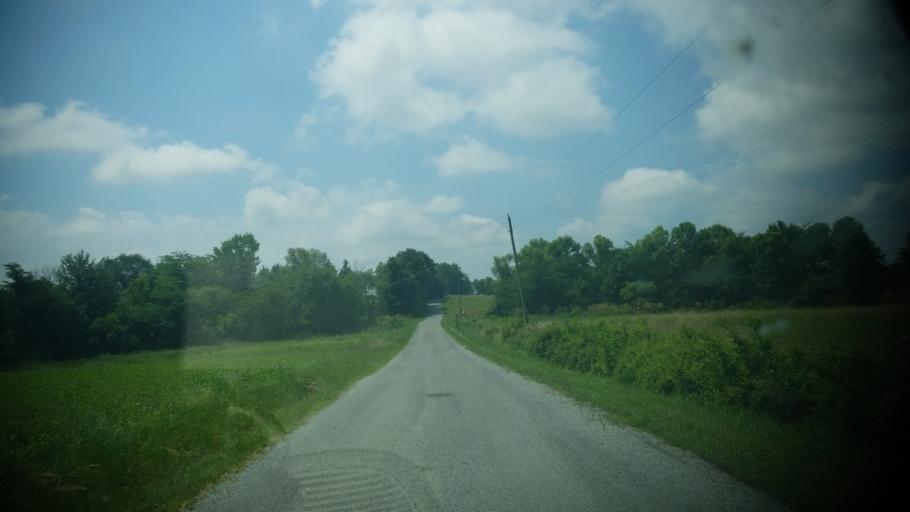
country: US
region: Illinois
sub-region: Wayne County
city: Fairfield
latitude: 38.5253
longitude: -88.3655
